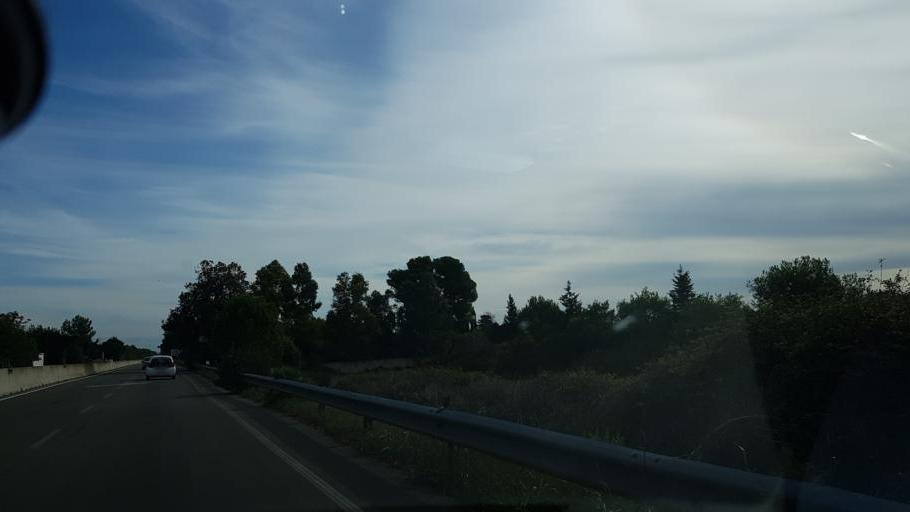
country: IT
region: Apulia
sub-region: Provincia di Lecce
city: Struda
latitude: 40.3807
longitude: 18.2710
